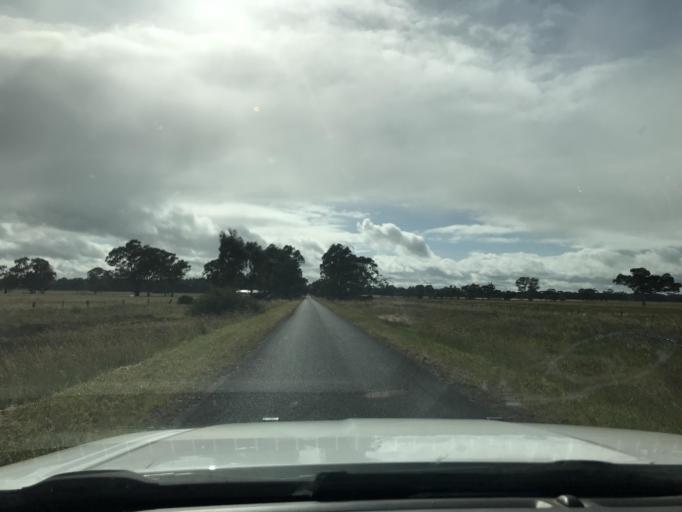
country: AU
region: South Australia
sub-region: Wattle Range
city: Penola
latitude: -37.1854
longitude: 141.2085
